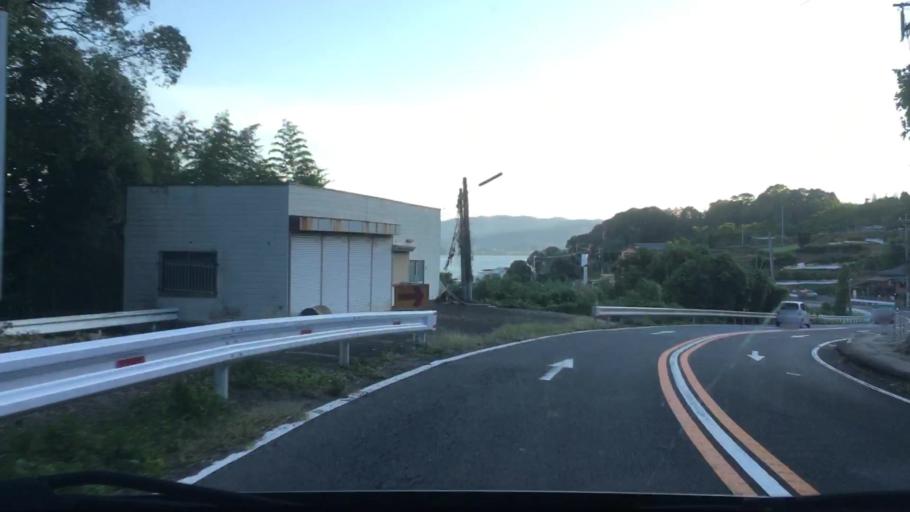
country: JP
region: Nagasaki
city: Sasebo
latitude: 33.0351
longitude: 129.7451
